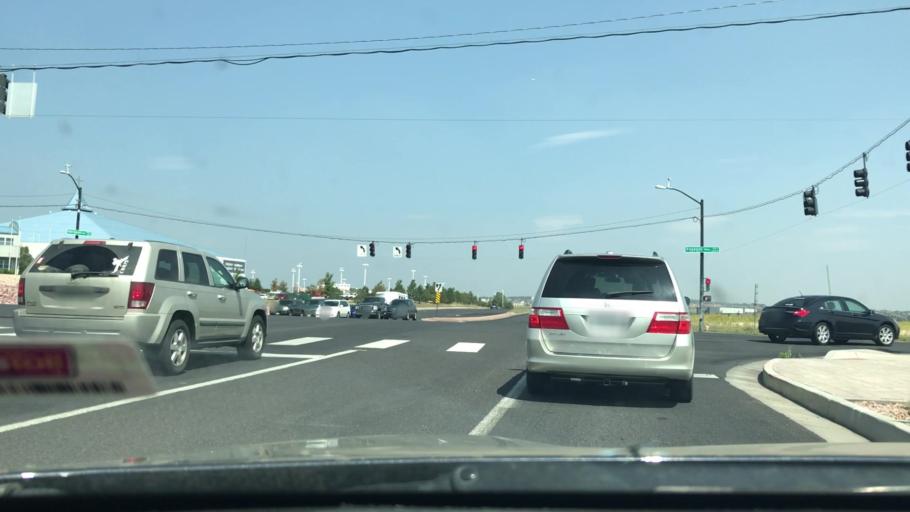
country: US
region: Colorado
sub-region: El Paso County
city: Gleneagle
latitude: 38.9906
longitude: -104.7985
